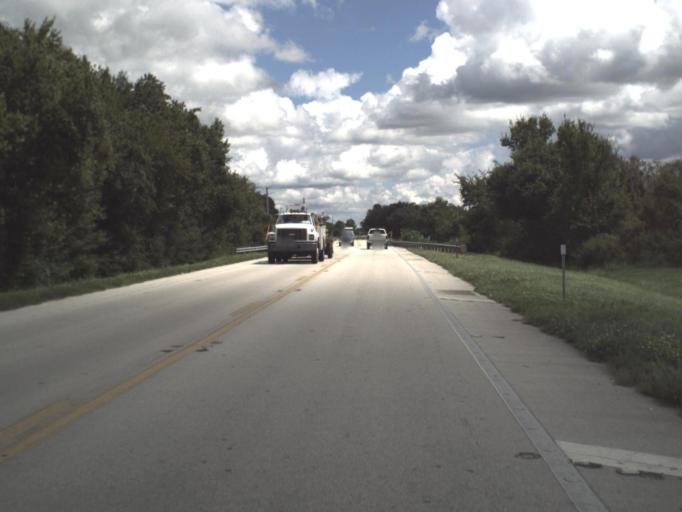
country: US
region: Florida
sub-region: DeSoto County
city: Southeast Arcadia
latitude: 27.2088
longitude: -81.8059
